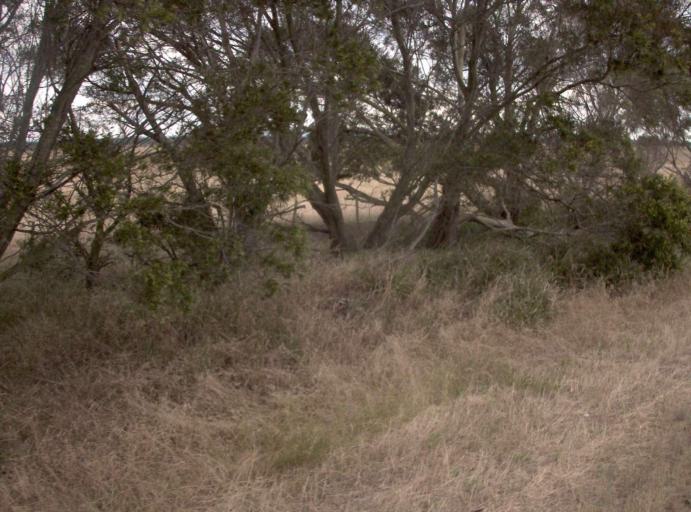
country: AU
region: Victoria
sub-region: East Gippsland
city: Bairnsdale
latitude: -37.9611
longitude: 147.4955
